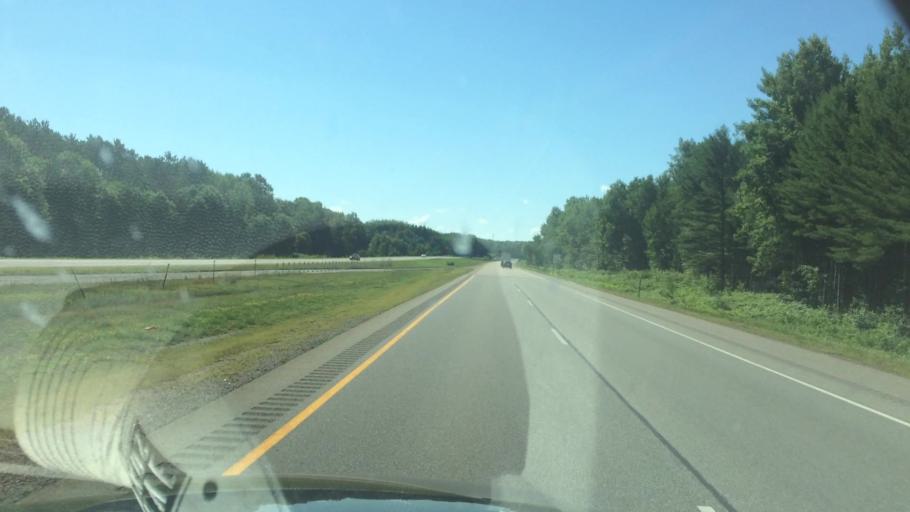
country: US
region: Wisconsin
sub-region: Marathon County
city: Mosinee
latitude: 44.7219
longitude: -89.6698
